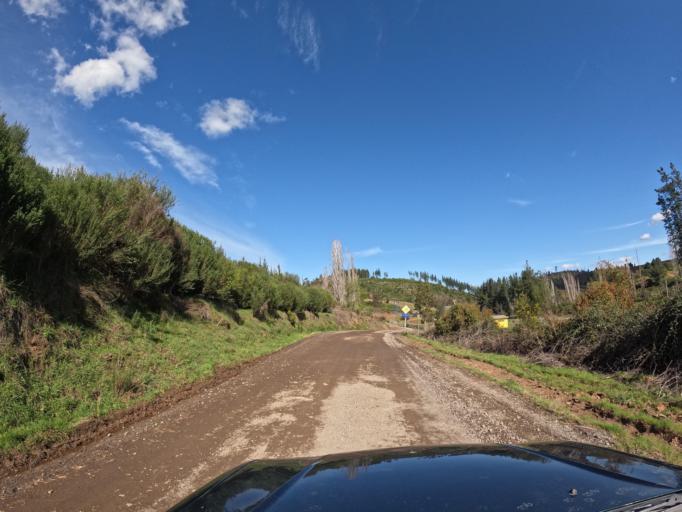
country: CL
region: Biobio
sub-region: Provincia de Concepcion
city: Chiguayante
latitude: -37.0686
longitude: -72.8480
